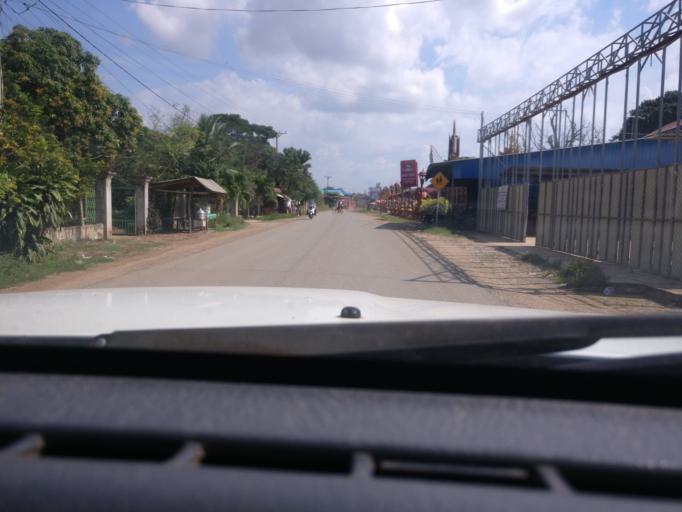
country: KH
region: Kandal
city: Ta Khmau
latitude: 11.4460
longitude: 105.0567
